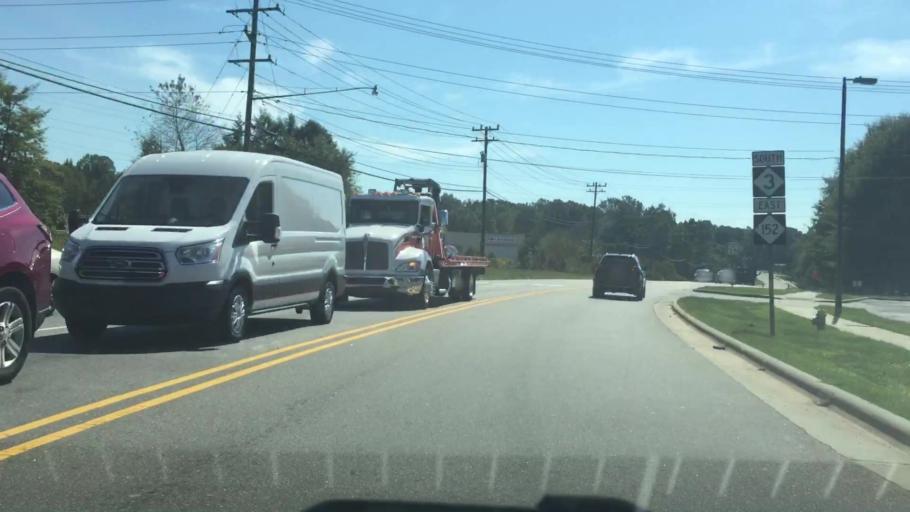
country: US
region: North Carolina
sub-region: Iredell County
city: Mooresville
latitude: 35.5951
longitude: -80.8164
